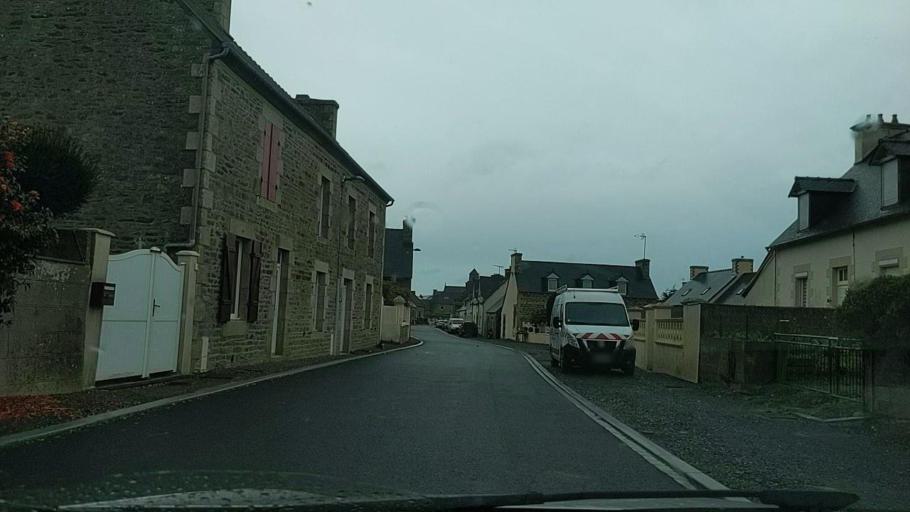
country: FR
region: Brittany
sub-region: Departement des Cotes-d'Armor
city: Pleumeur-Gautier
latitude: 48.8004
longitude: -3.1570
